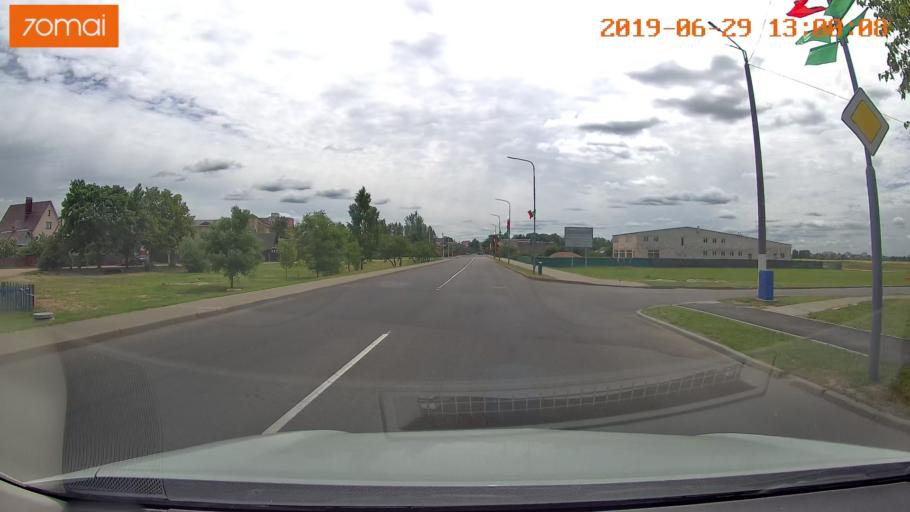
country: BY
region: Minsk
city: Slutsk
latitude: 53.0470
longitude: 27.5558
